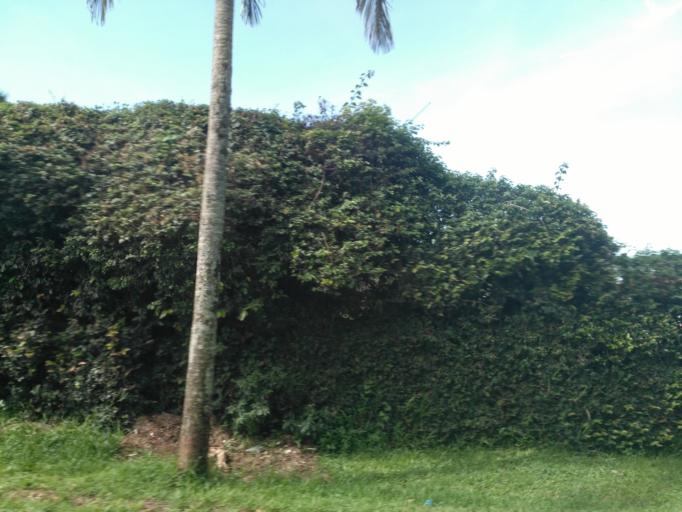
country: UG
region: Central Region
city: Kampala Central Division
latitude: 0.3270
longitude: 32.5781
